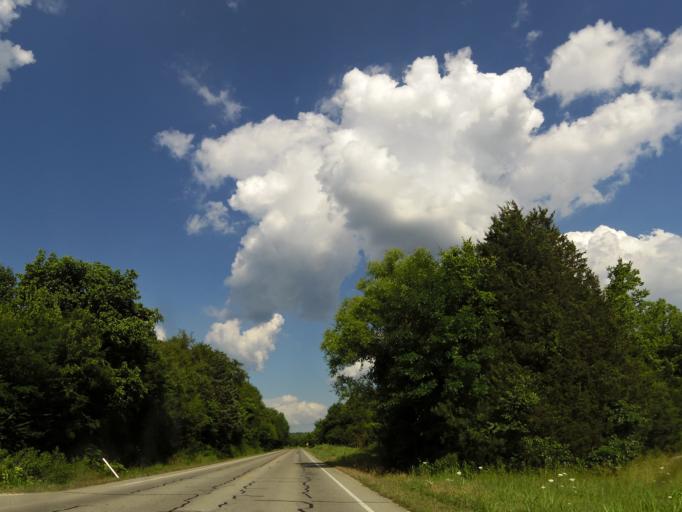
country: US
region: Tennessee
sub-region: Perry County
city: Linden
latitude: 35.6334
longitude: -87.7745
